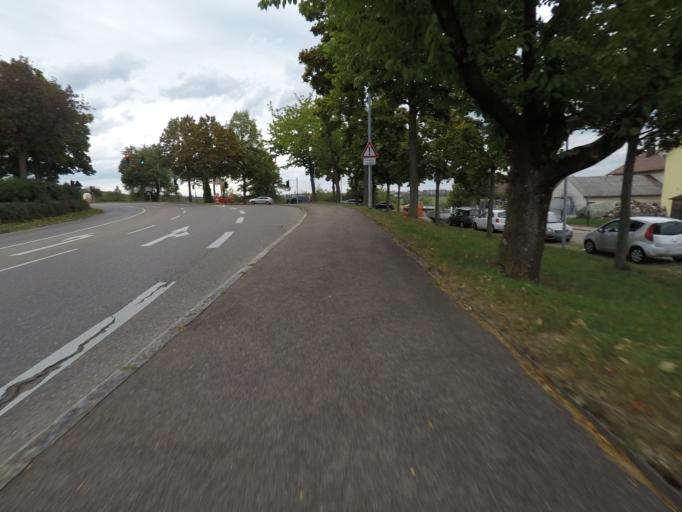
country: DE
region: Baden-Wuerttemberg
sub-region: Regierungsbezirk Stuttgart
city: Leinfelden-Echterdingen
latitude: 48.6709
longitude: 9.1745
